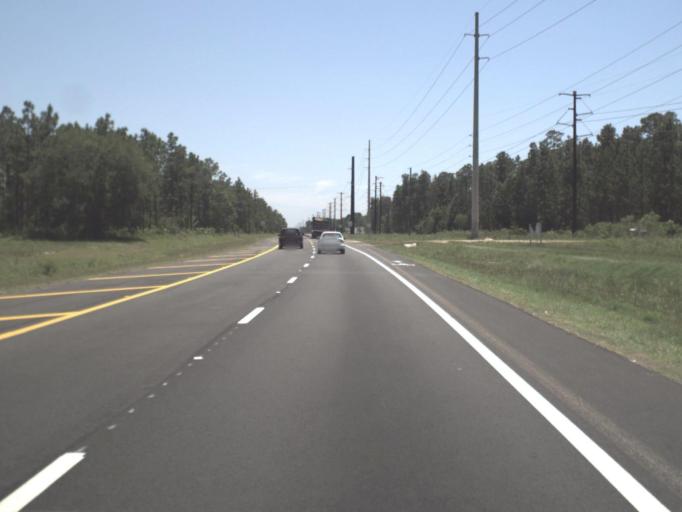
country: US
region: Florida
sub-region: Clay County
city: Lakeside
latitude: 30.1579
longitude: -81.8317
